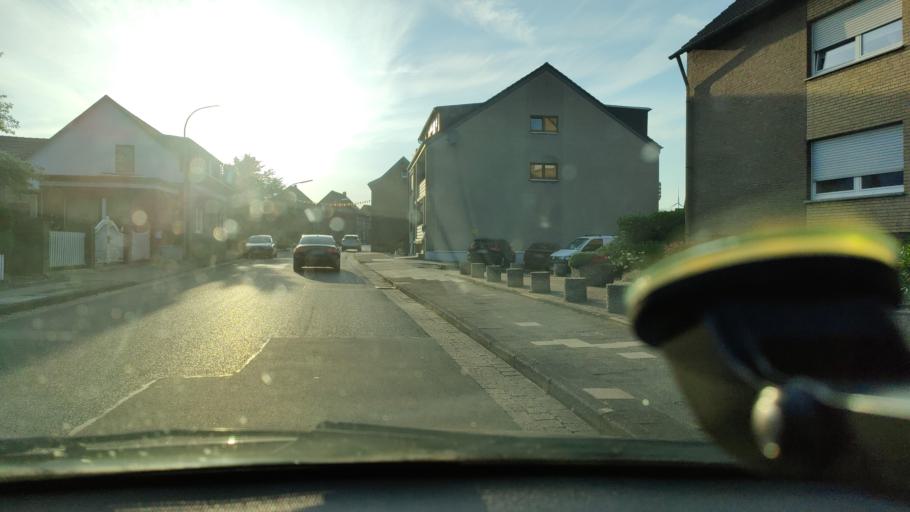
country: DE
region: North Rhine-Westphalia
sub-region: Regierungsbezirk Dusseldorf
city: Rheurdt
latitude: 51.4641
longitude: 6.4738
